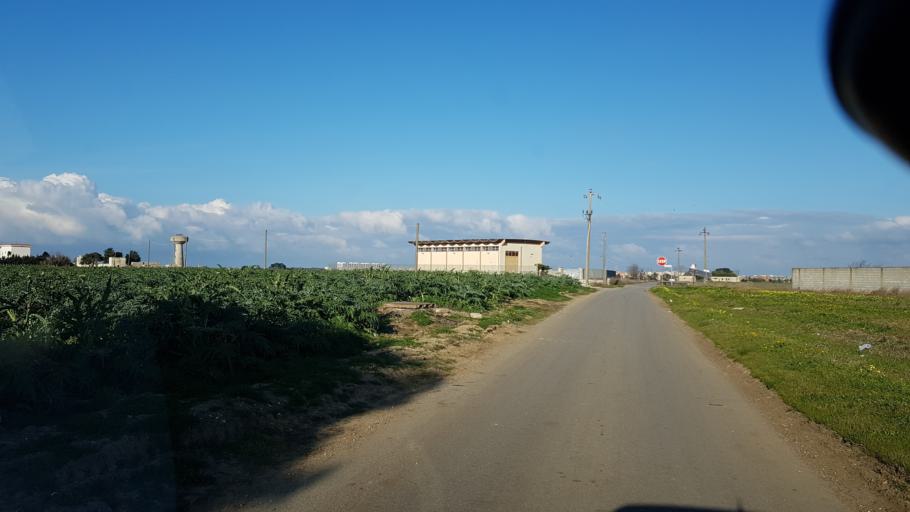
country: IT
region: Apulia
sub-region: Provincia di Brindisi
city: Brindisi
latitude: 40.6031
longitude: 17.9069
